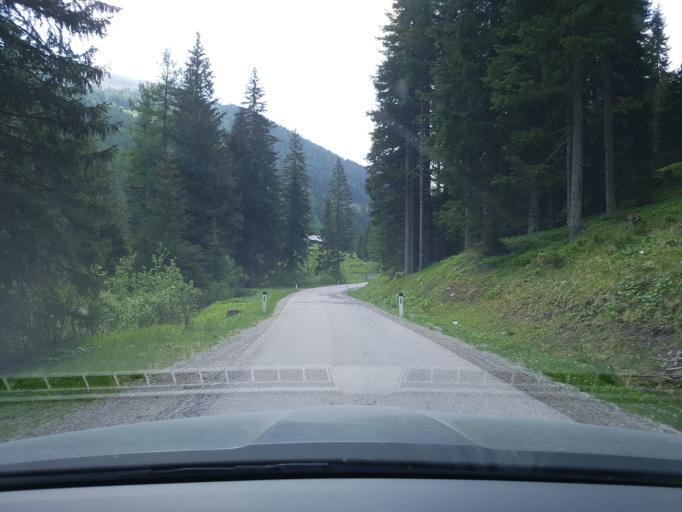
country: AT
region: Salzburg
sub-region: Politischer Bezirk Tamsweg
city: Thomatal
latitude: 47.0296
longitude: 13.7575
